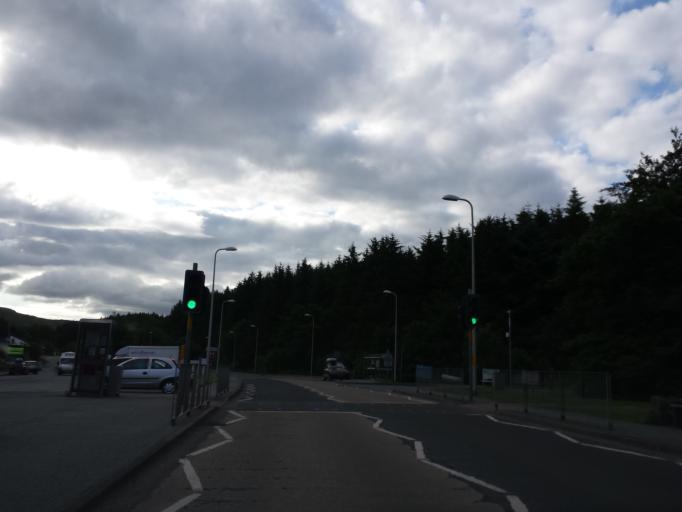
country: GB
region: Scotland
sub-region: Highland
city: Portree
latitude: 57.2428
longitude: -5.9132
